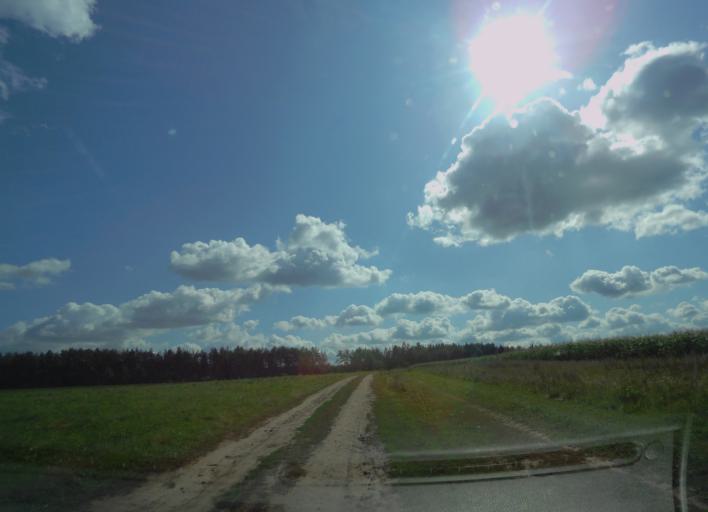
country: BY
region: Minsk
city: Zyembin
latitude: 54.3859
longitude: 28.3853
